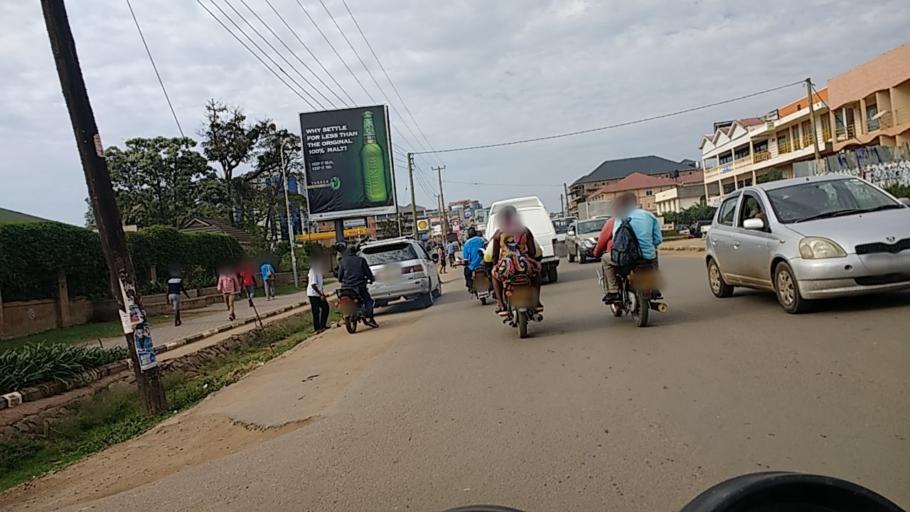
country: UG
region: Western Region
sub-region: Mbarara District
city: Mbarara
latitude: -0.5997
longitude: 30.6638
